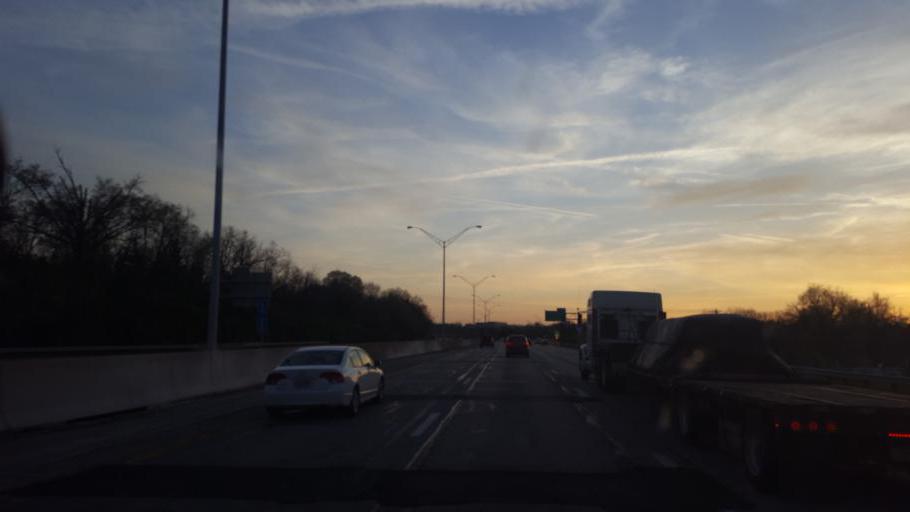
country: US
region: Ohio
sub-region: Hamilton County
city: Norwood
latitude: 39.1484
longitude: -84.4497
